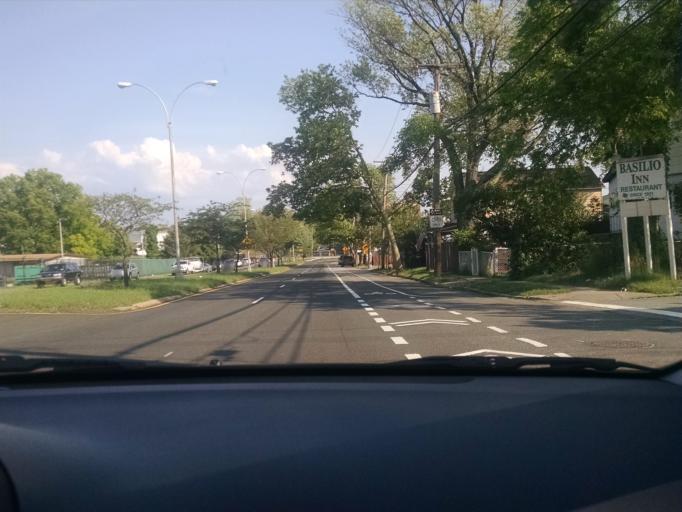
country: US
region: New York
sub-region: Kings County
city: Bensonhurst
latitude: 40.5979
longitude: -74.0630
